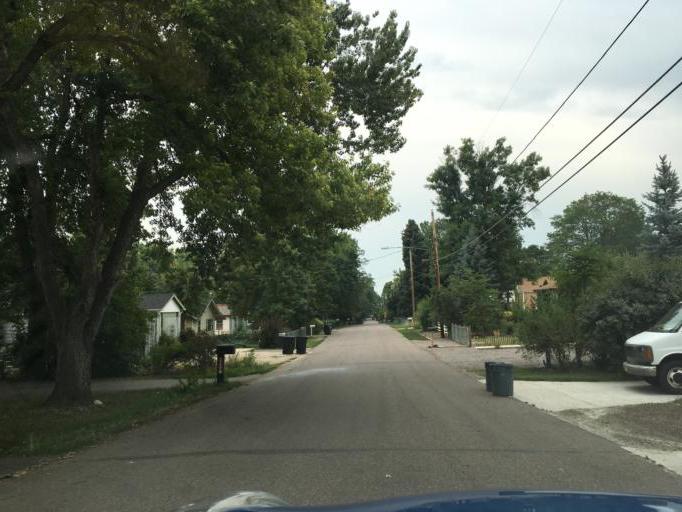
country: US
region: Colorado
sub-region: Jefferson County
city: Wheat Ridge
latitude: 39.7510
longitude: -105.1001
